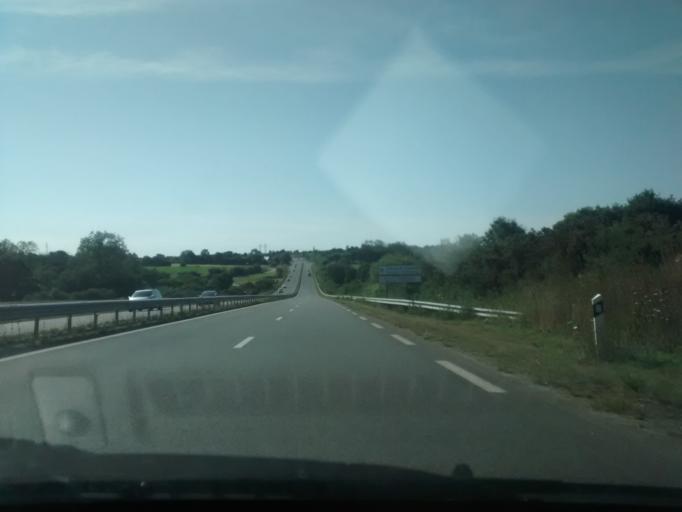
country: FR
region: Brittany
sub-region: Departement des Cotes-d'Armor
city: Rospez
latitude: 48.7107
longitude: -3.3865
